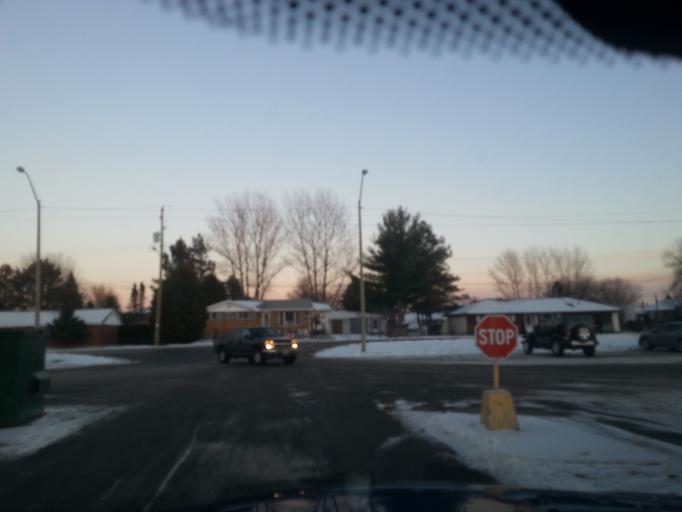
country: CA
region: Ontario
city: Greater Sudbury
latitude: 46.6512
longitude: -80.9880
